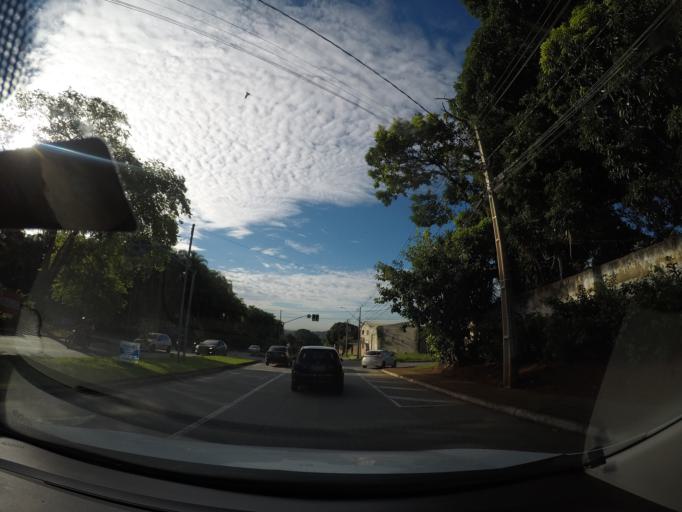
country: BR
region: Goias
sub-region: Goiania
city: Goiania
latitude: -16.7426
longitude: -49.2709
